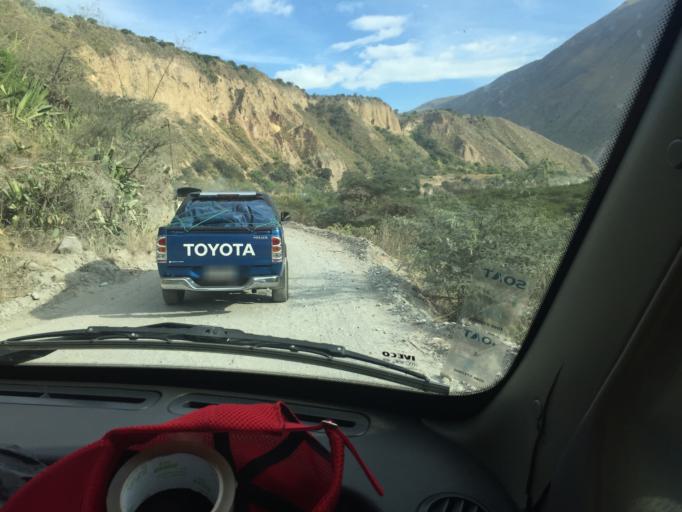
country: EC
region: Carchi
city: El Angel
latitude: 0.5990
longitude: -78.1378
